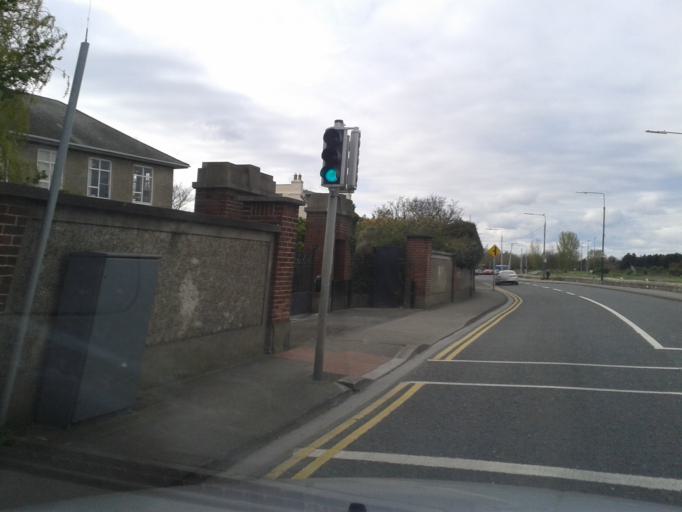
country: IE
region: Leinster
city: Sandymount
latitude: 53.3332
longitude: -6.2113
